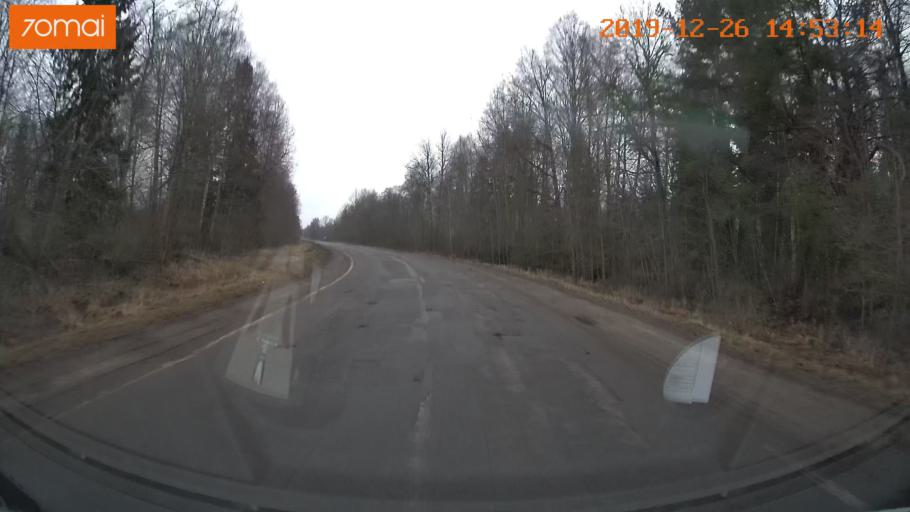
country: RU
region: Jaroslavl
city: Rybinsk
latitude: 58.3167
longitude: 38.8908
